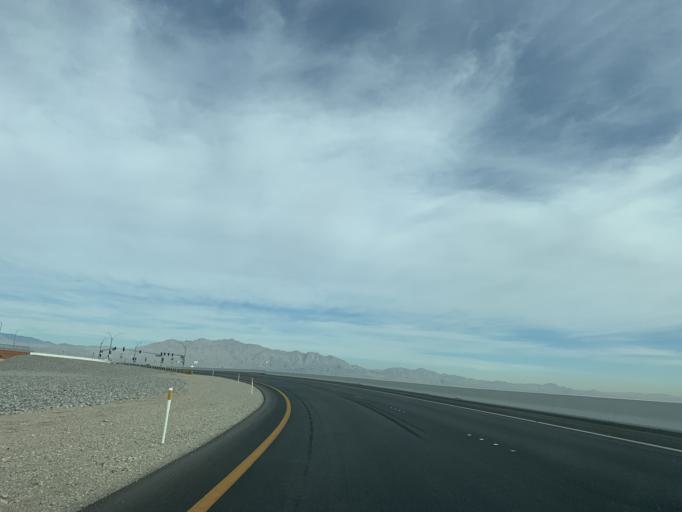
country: US
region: Nevada
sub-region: Clark County
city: Summerlin South
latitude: 36.2459
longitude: -115.3182
